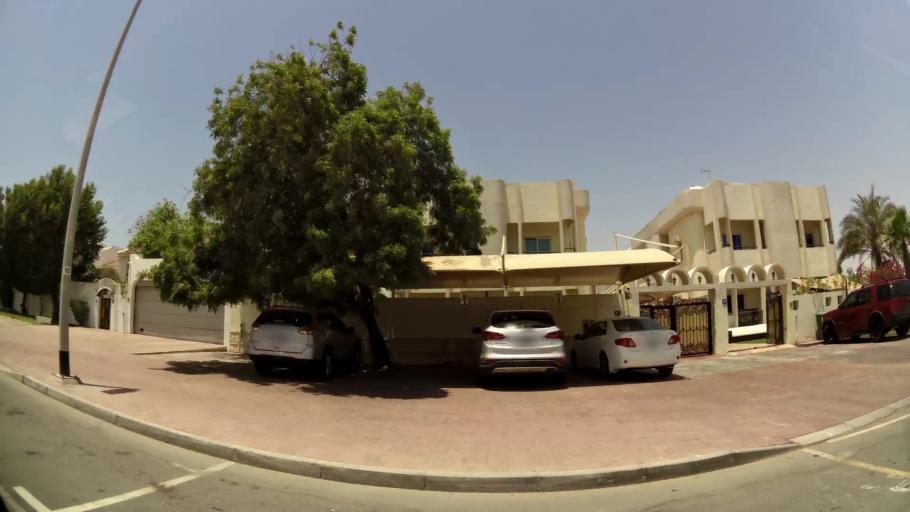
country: AE
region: Dubai
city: Dubai
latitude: 25.2060
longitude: 55.2476
